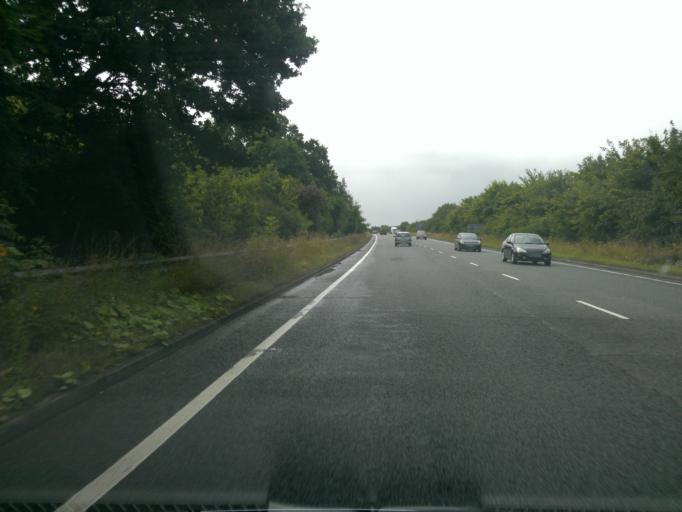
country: GB
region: England
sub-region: Essex
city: Little Clacton
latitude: 51.8183
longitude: 1.1376
